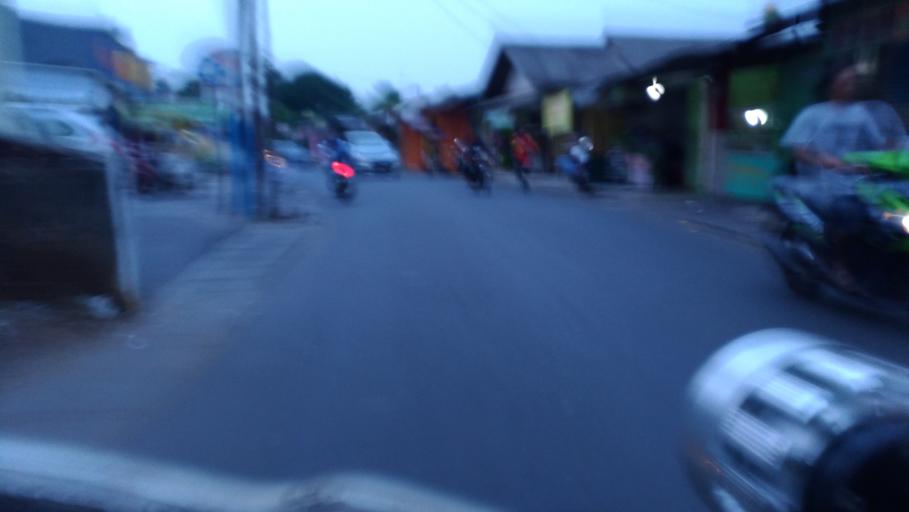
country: ID
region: West Java
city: Depok
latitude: -6.3602
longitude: 106.8835
